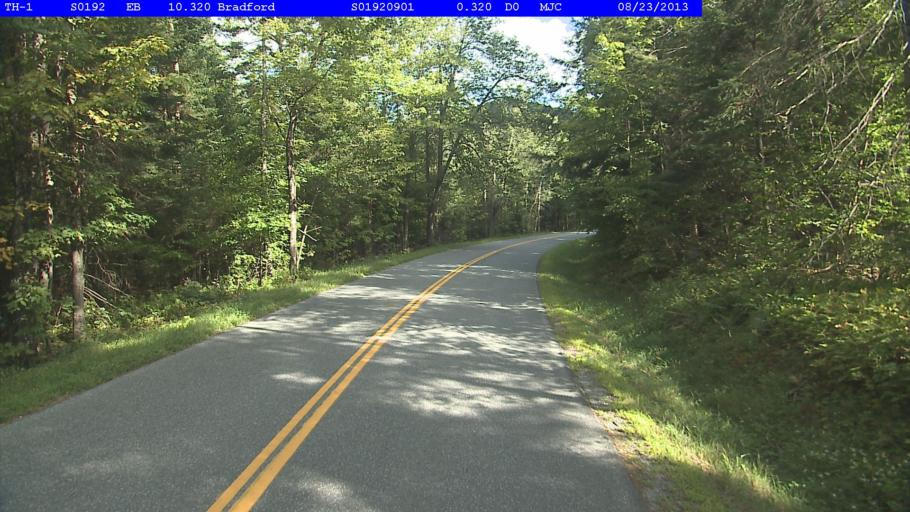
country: US
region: New Hampshire
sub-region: Grafton County
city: Orford
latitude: 44.0206
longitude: -72.2097
